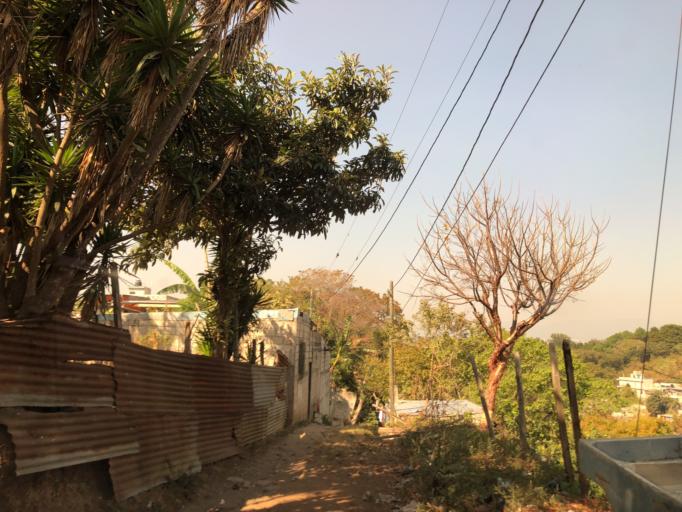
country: GT
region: Guatemala
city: Santa Catarina Pinula
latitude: 14.5396
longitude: -90.5174
